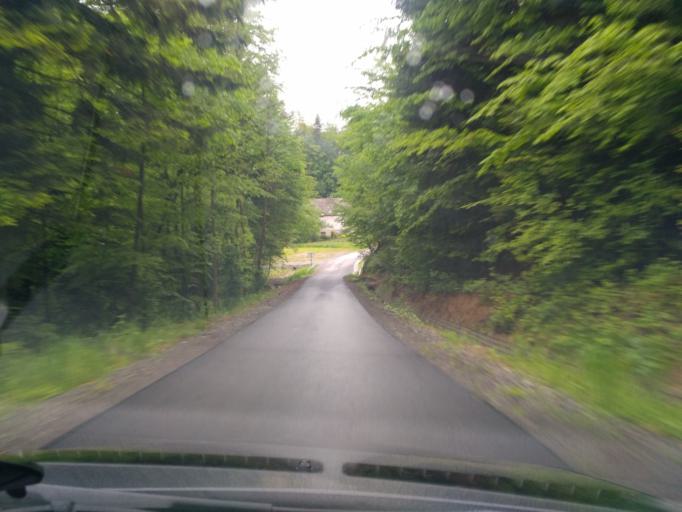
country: PL
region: Subcarpathian Voivodeship
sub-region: Powiat debicki
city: Jodlowa
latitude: 49.8672
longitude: 21.2317
